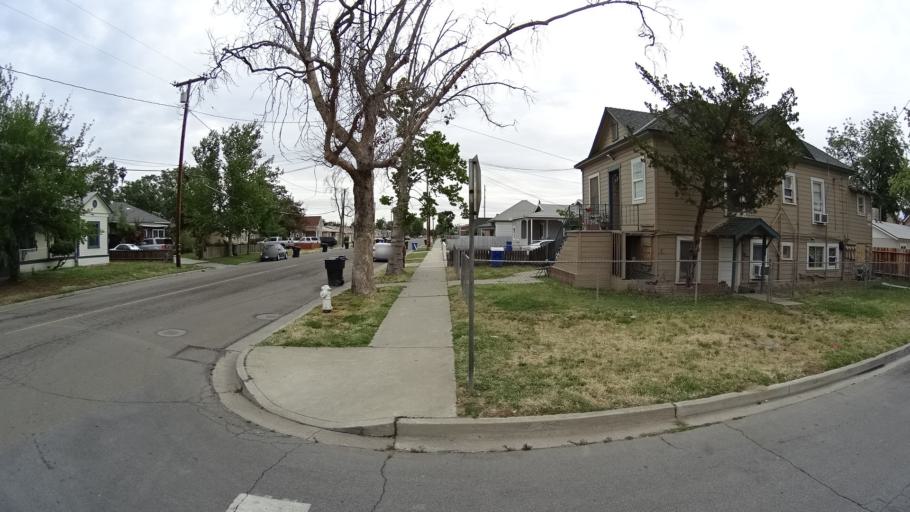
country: US
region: California
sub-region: Kings County
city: Hanford
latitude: 36.3330
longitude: -119.6427
